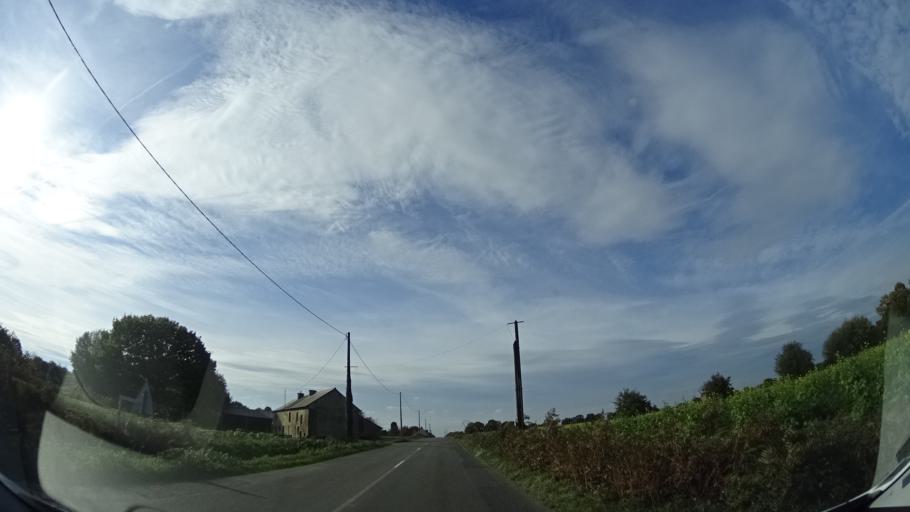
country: FR
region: Brittany
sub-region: Departement d'Ille-et-Vilaine
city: Romille
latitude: 48.2166
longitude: -1.8618
